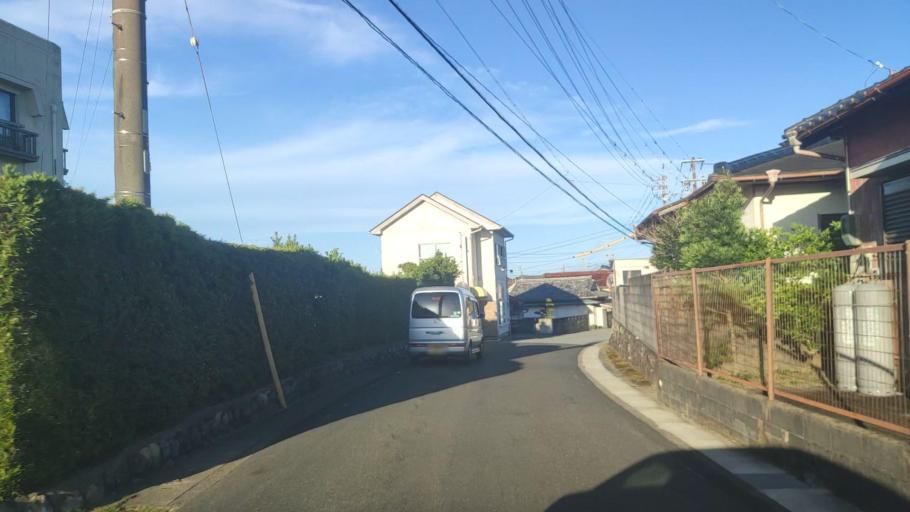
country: JP
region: Mie
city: Toba
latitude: 34.2553
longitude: 136.8302
